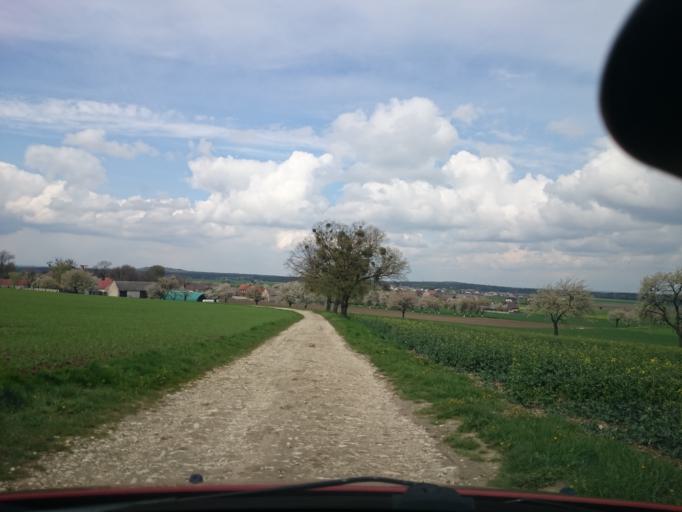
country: PL
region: Opole Voivodeship
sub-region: Powiat krapkowicki
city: Rozwadza
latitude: 50.4886
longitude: 18.1254
